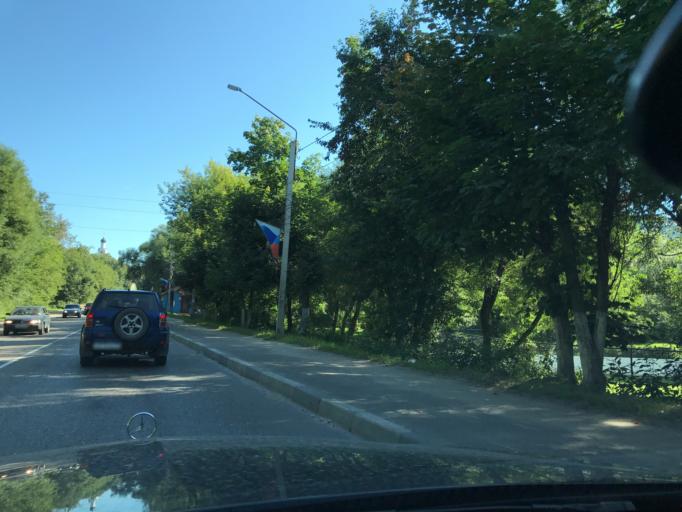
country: RU
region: Vladimir
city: Kirzhach
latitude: 56.1574
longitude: 38.8647
